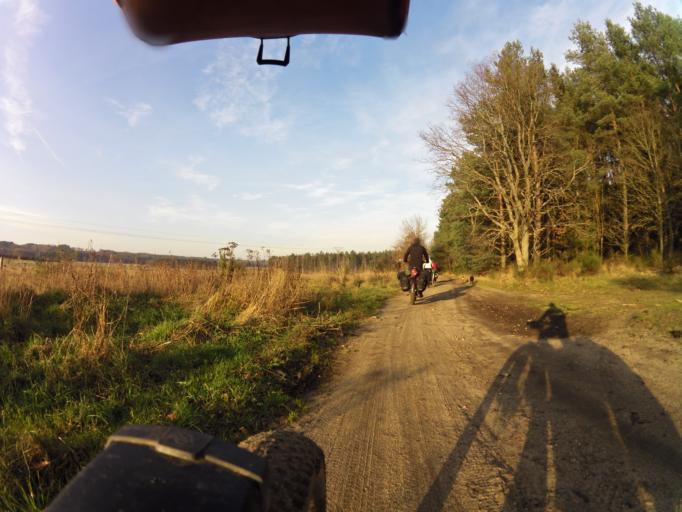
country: PL
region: West Pomeranian Voivodeship
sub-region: Powiat koszalinski
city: Polanow
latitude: 54.0973
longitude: 16.6482
